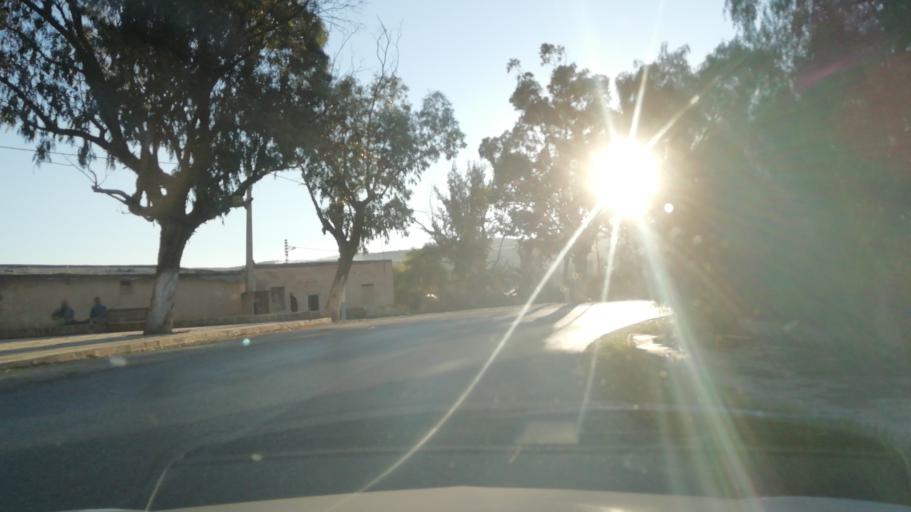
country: DZ
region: Tlemcen
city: Nedroma
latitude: 34.8256
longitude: -1.6508
